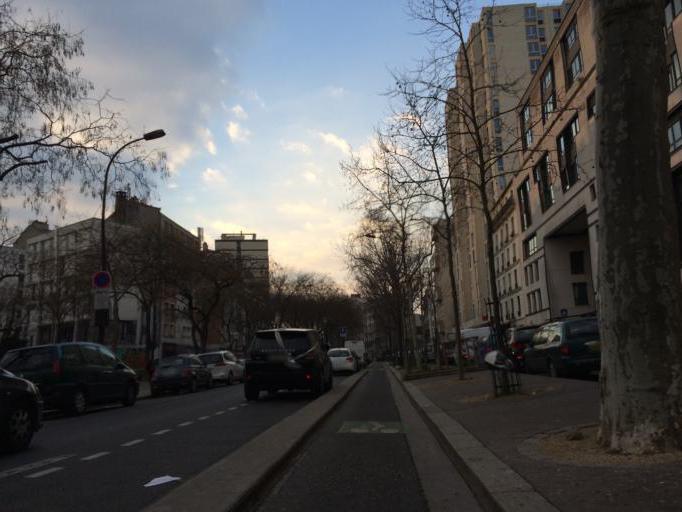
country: FR
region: Ile-de-France
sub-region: Departement de Seine-Saint-Denis
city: Bagnolet
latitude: 48.8568
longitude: 2.3941
